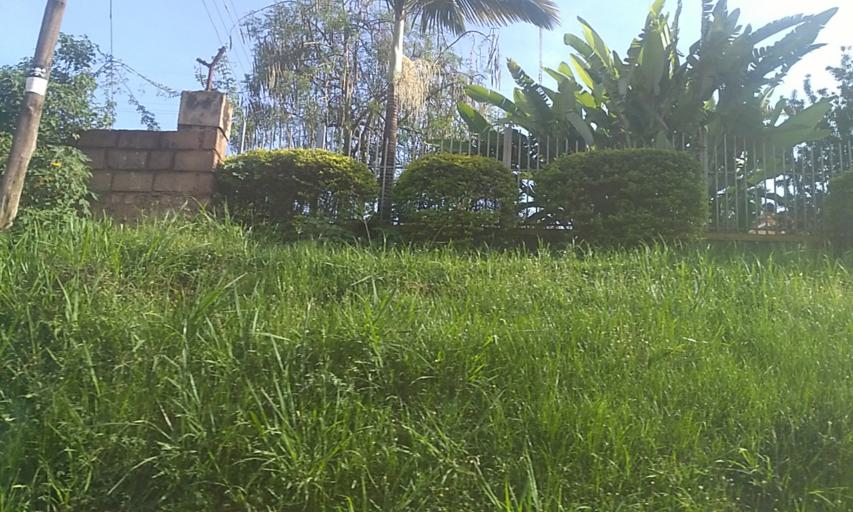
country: UG
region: Central Region
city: Kampala Central Division
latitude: 0.3501
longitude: 32.6045
